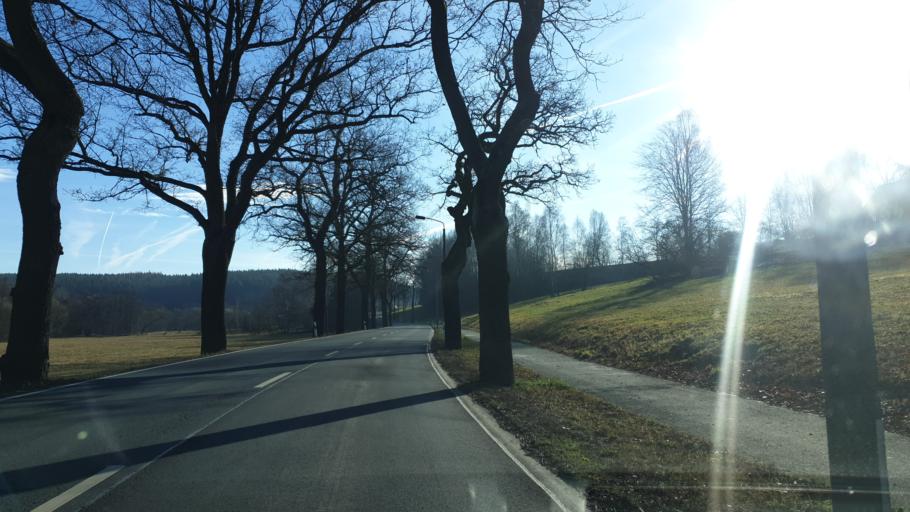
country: DE
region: Saxony
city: Adorf
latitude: 50.2930
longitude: 12.2686
